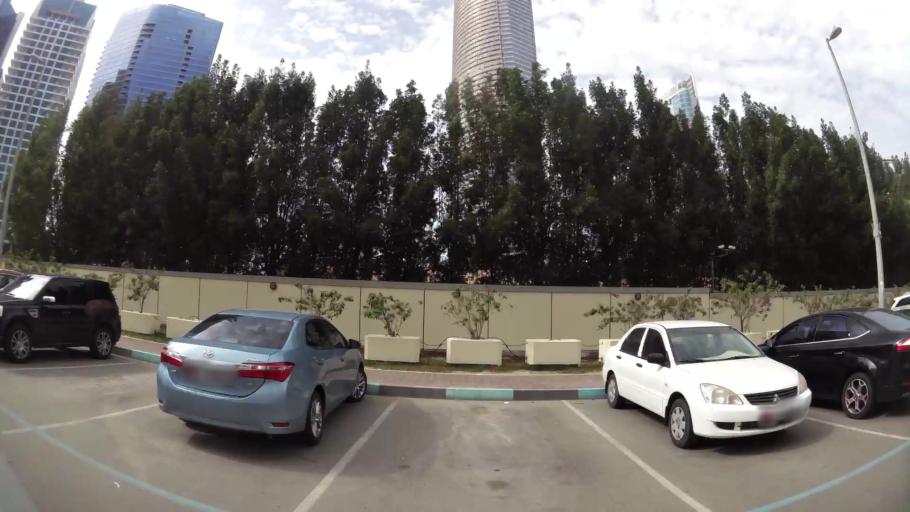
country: AE
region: Abu Dhabi
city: Abu Dhabi
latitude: 24.4830
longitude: 54.3522
